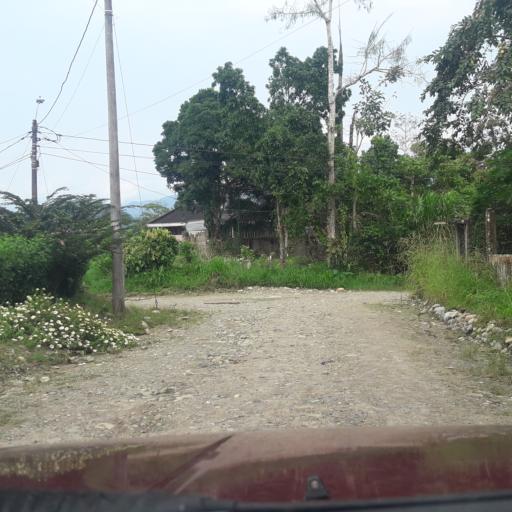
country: EC
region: Napo
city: Tena
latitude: -0.9814
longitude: -77.8154
